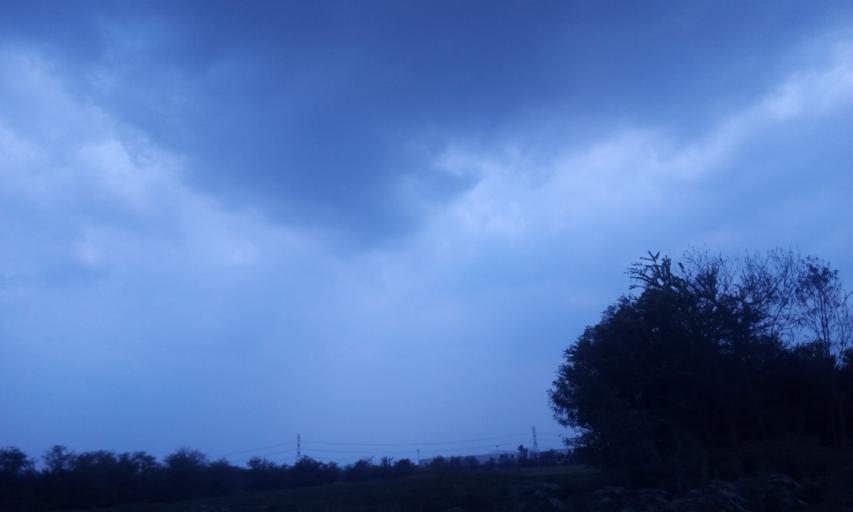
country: TH
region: Chon Buri
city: Ban Bueng
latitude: 13.2958
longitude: 101.1772
